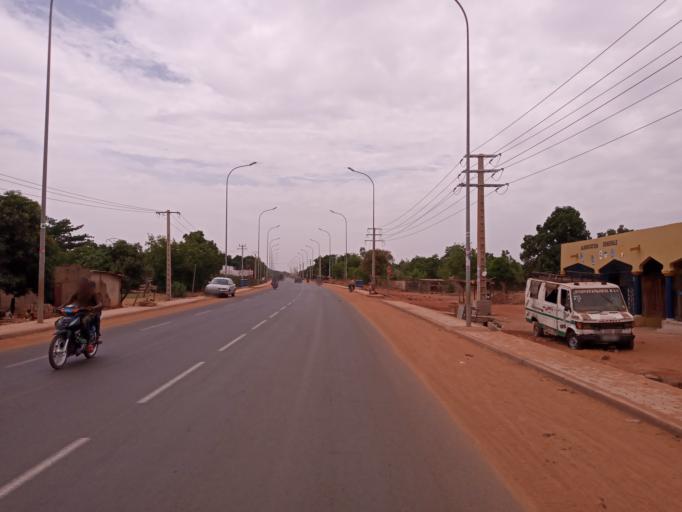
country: ML
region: Koulikoro
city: Koulikoro
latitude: 12.8522
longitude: -7.5697
